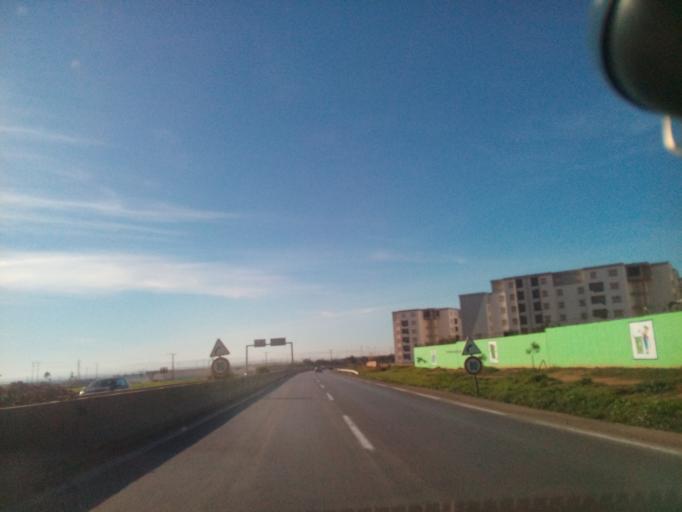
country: DZ
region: Oran
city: Ain el Bya
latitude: 35.7819
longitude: -0.4129
